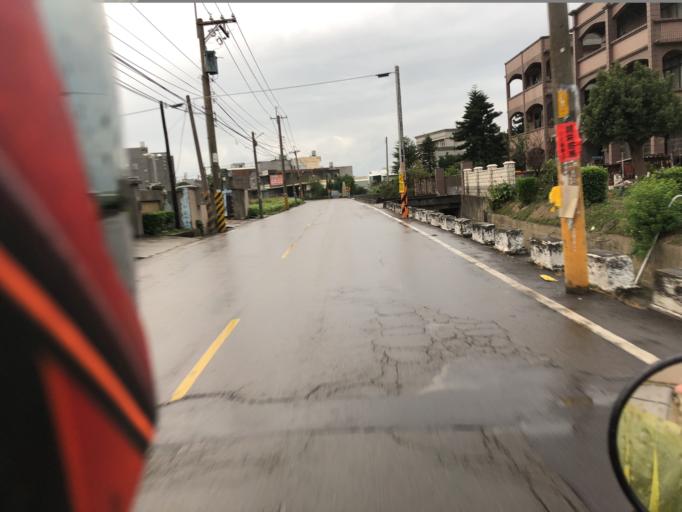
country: TW
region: Taiwan
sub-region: Hsinchu
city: Zhubei
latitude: 24.8460
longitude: 120.9903
